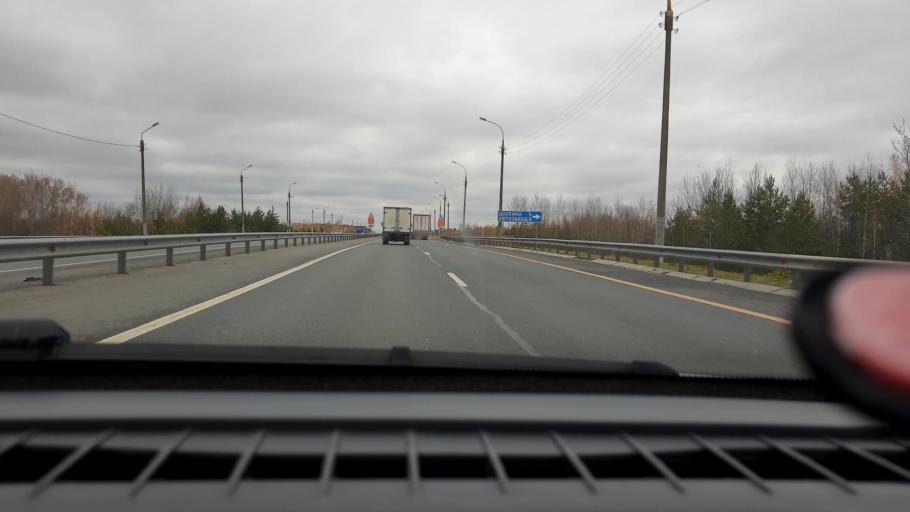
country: RU
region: Nizjnij Novgorod
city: Gorbatovka
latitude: 56.2572
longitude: 43.7099
